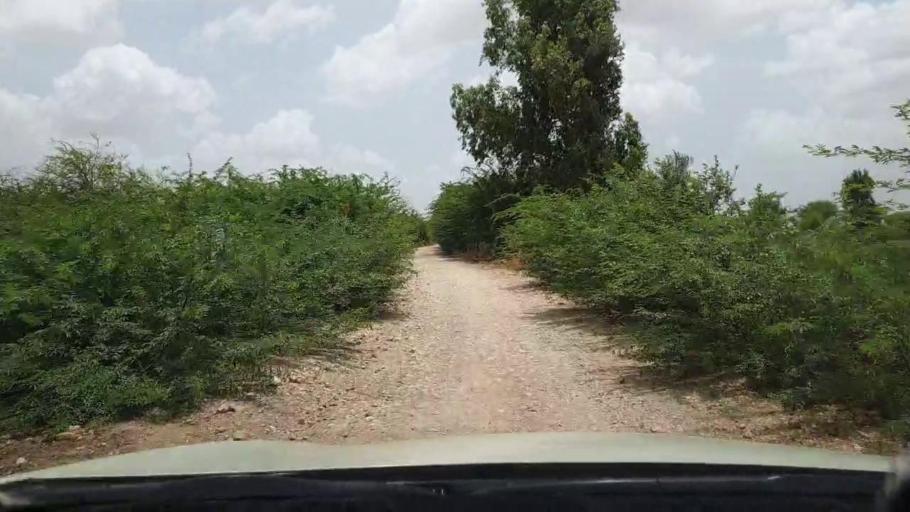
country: PK
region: Sindh
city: Kadhan
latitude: 24.3753
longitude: 68.9286
